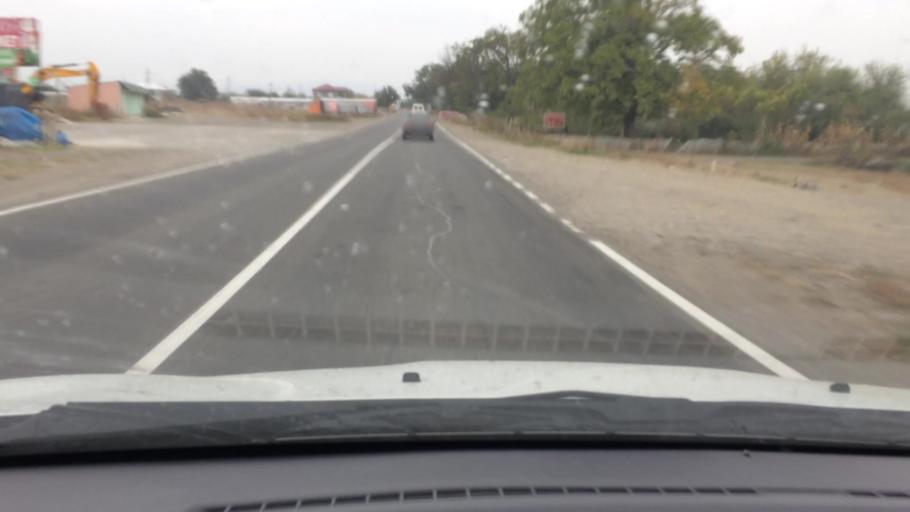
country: GE
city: Naghvarevi
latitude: 41.3950
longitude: 44.8275
